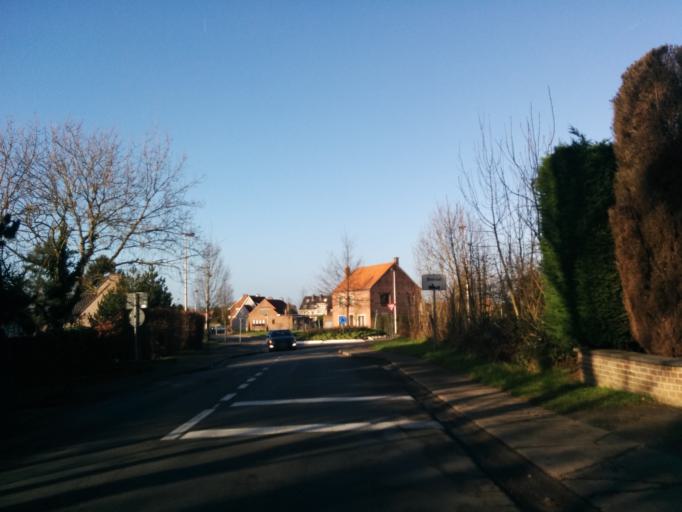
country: BE
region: Flanders
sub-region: Provincie Vlaams-Brabant
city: Beersel
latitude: 50.7577
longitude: 4.3065
